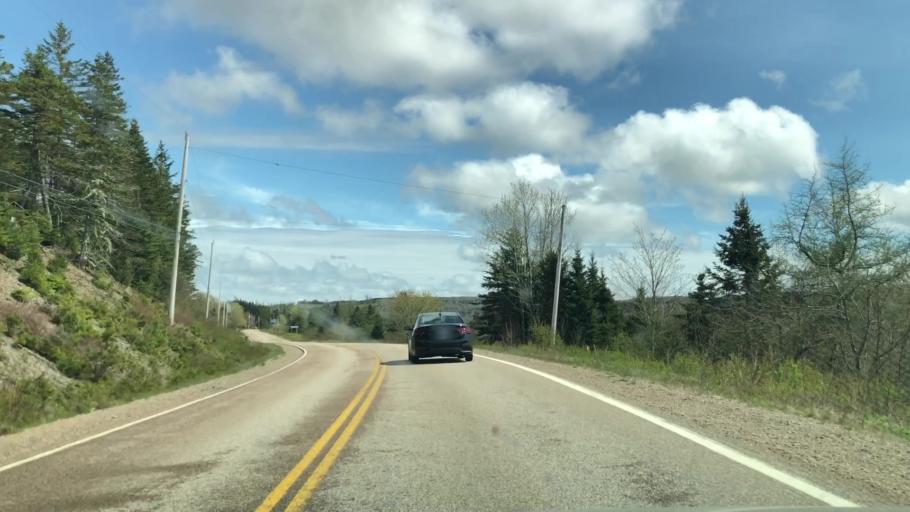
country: CA
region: Nova Scotia
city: Antigonish
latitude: 45.1888
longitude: -61.9884
